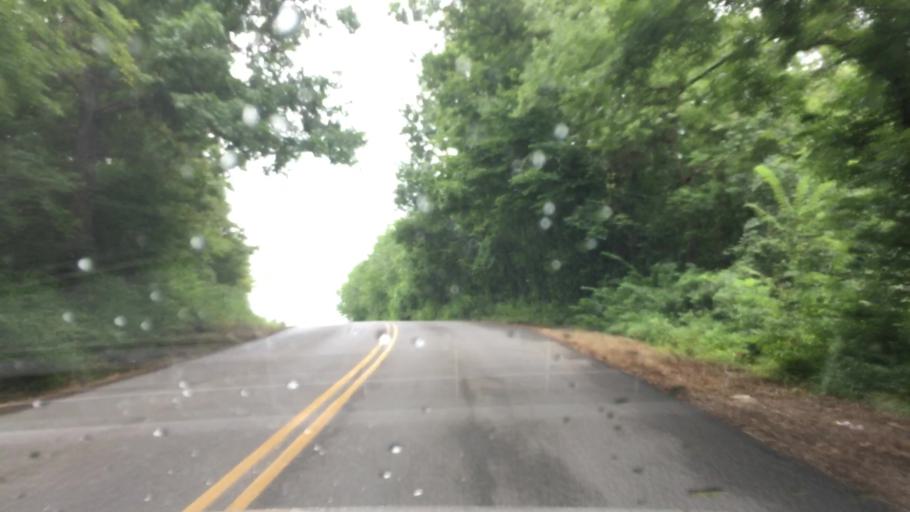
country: US
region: Oklahoma
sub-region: Muskogee County
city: Fort Gibson
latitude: 35.8980
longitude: -95.1627
